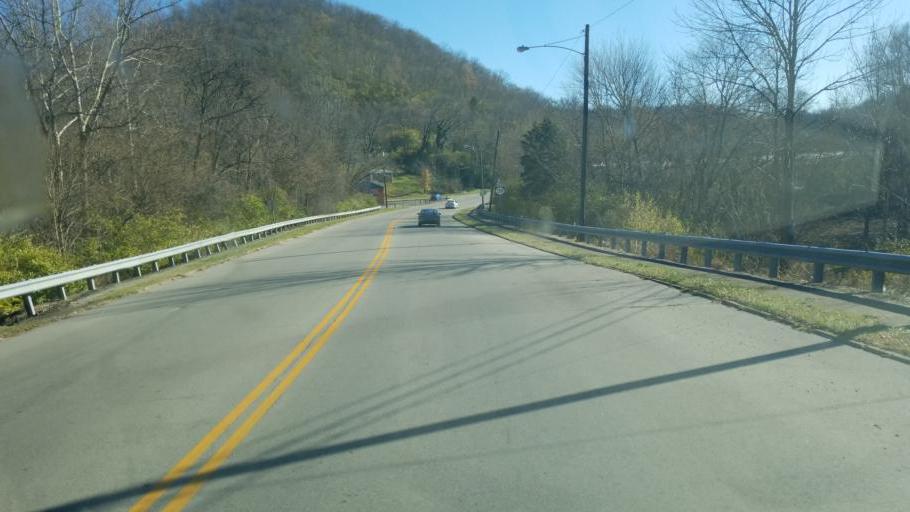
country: US
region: Kentucky
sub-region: Mason County
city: Maysville
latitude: 38.6387
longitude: -83.7557
